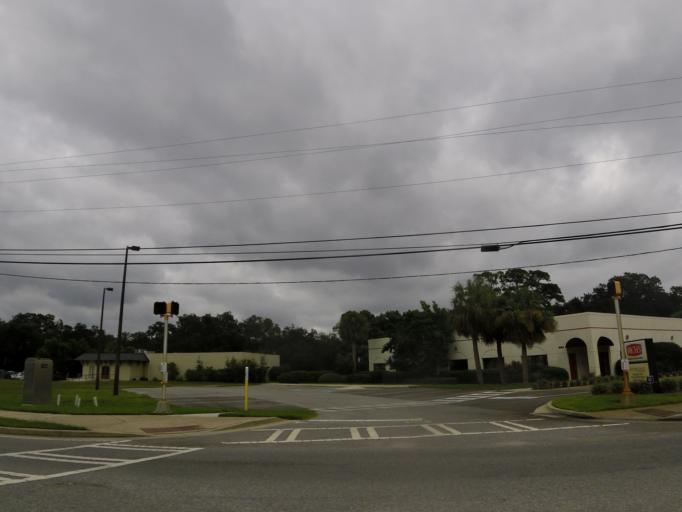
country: US
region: Georgia
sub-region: Glynn County
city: Saint Simons Island
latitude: 31.1557
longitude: -81.3861
